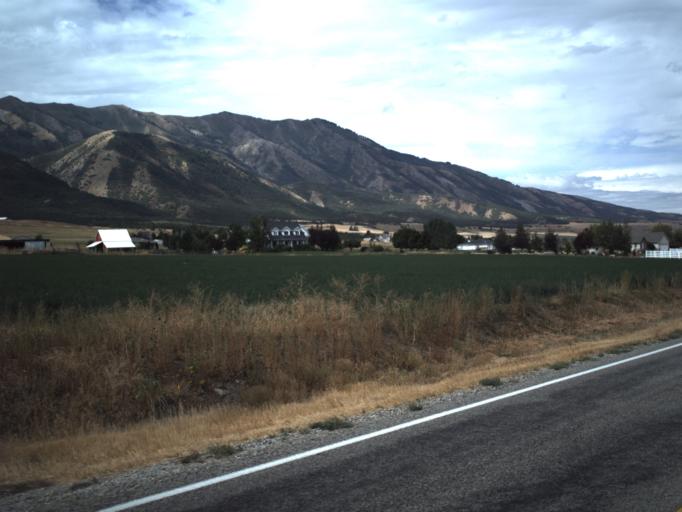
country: US
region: Utah
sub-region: Cache County
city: Wellsville
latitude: 41.6599
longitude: -111.9460
